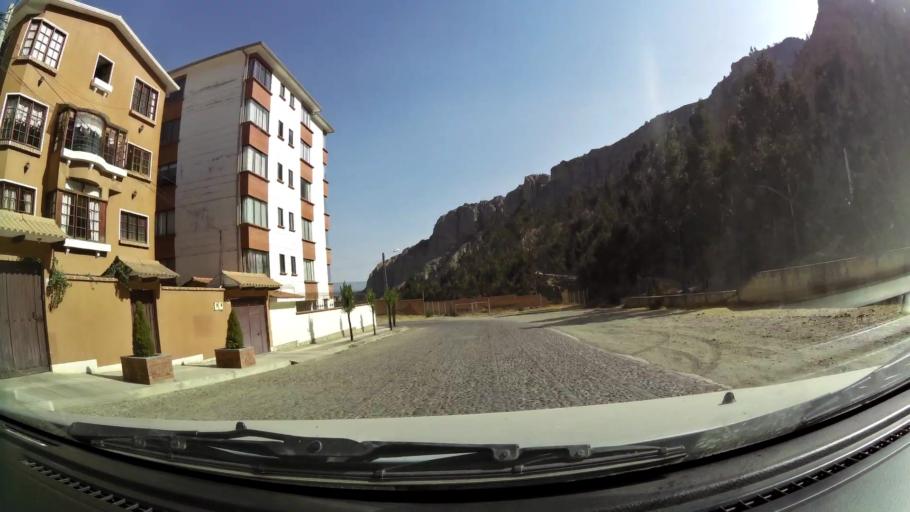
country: BO
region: La Paz
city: La Paz
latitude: -16.5139
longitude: -68.0636
